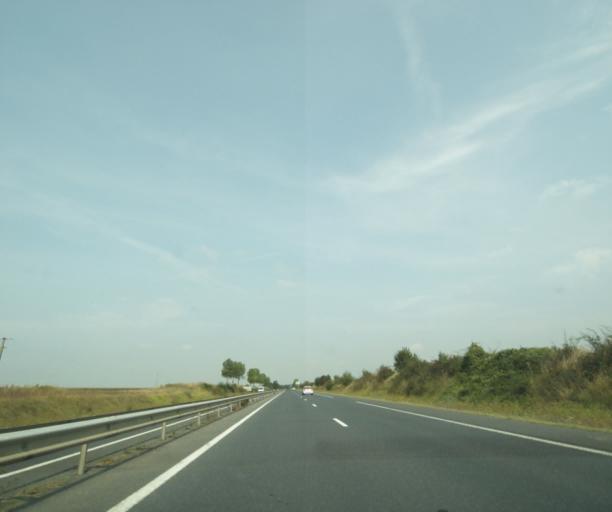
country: FR
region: Lower Normandy
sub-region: Departement du Calvados
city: Potigny
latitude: 49.0002
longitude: -0.2573
